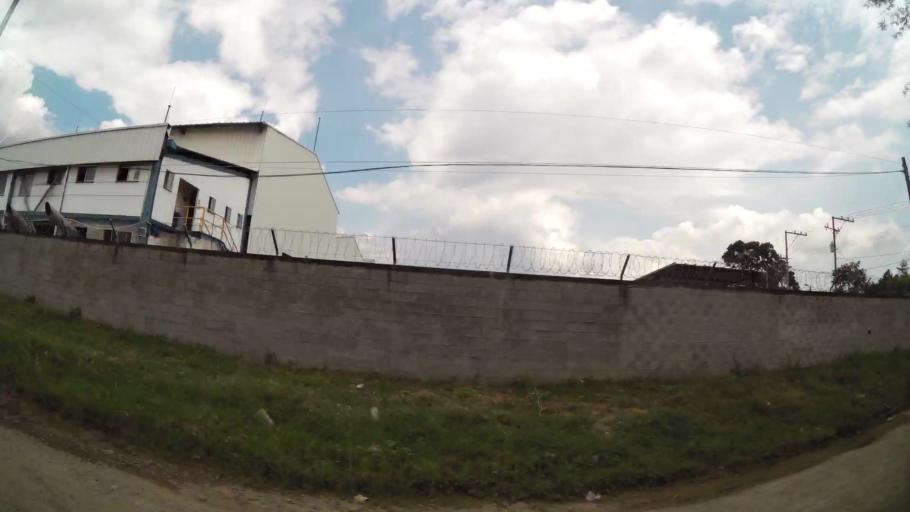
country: CO
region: Valle del Cauca
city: Cali
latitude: 3.4952
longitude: -76.4815
